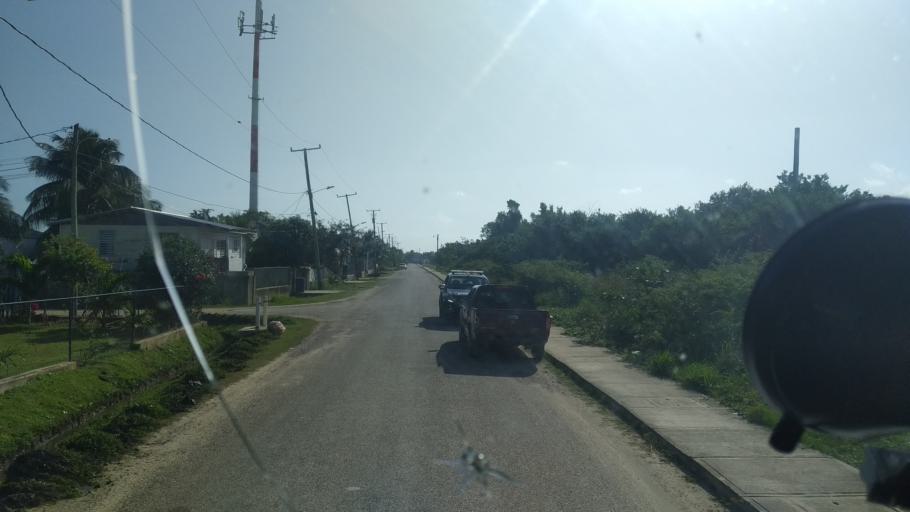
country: BZ
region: Belize
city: Belize City
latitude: 17.4843
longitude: -88.2067
